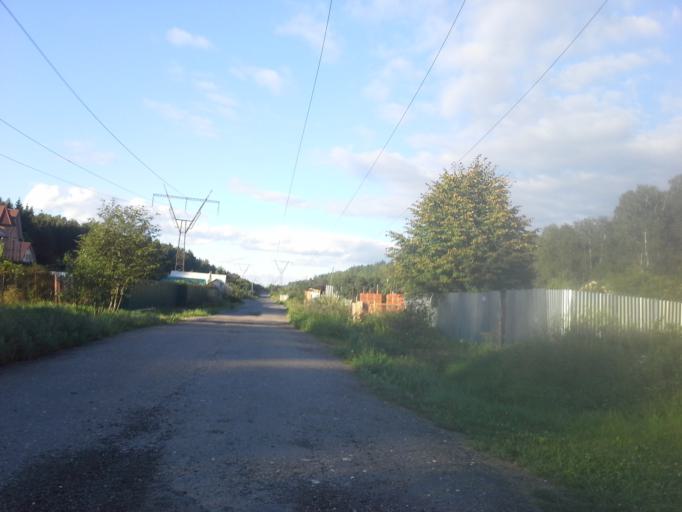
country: RU
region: Moskovskaya
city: Kievskij
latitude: 55.4687
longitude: 36.8633
